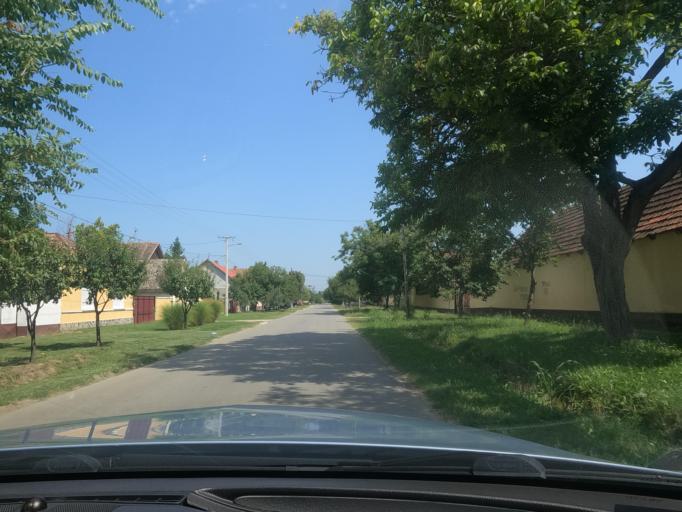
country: RS
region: Autonomna Pokrajina Vojvodina
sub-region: Juznobacki Okrug
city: Kovilj
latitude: 45.2219
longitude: 20.0301
